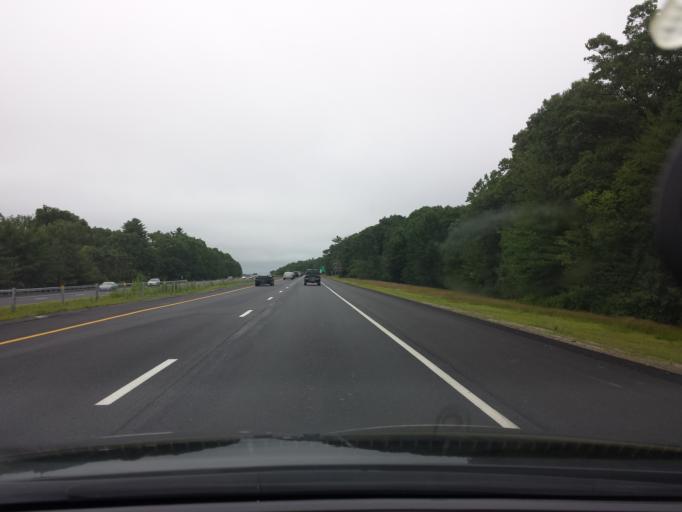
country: US
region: Rhode Island
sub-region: Kent County
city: West Greenwich
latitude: 41.5800
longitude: -71.6602
